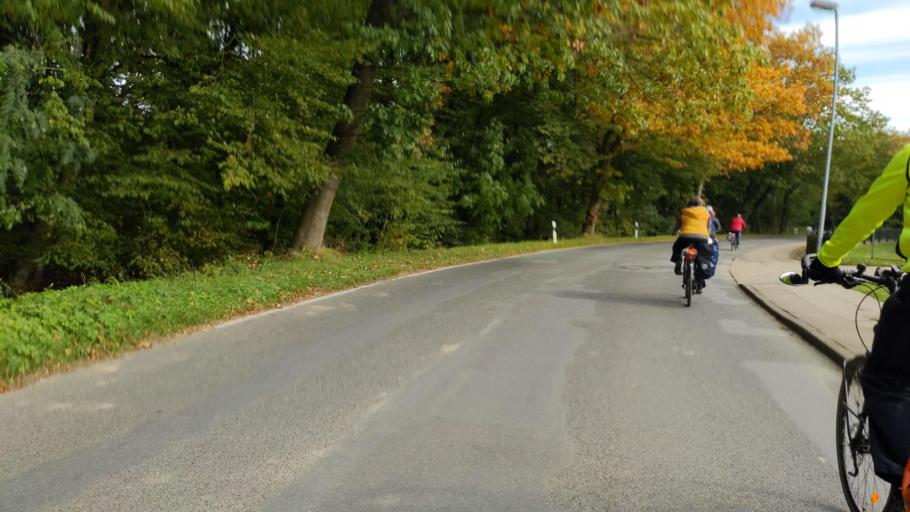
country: DE
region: Schleswig-Holstein
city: Meddewade
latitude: 53.8343
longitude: 10.4622
